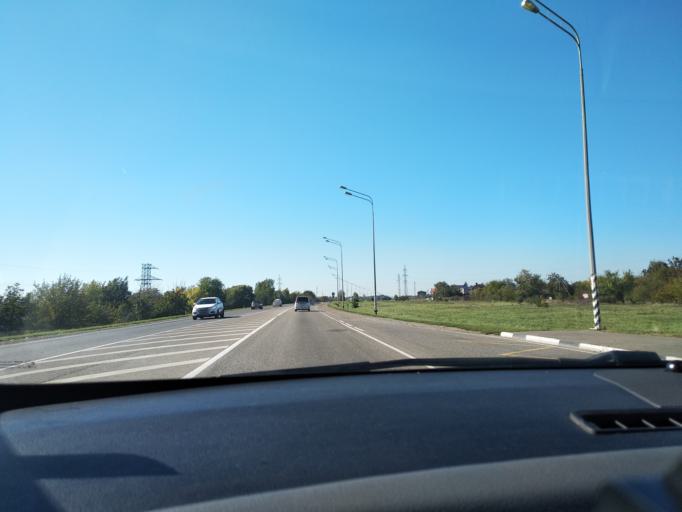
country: RU
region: Krasnodarskiy
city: Agronom
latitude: 45.1625
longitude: 39.0827
